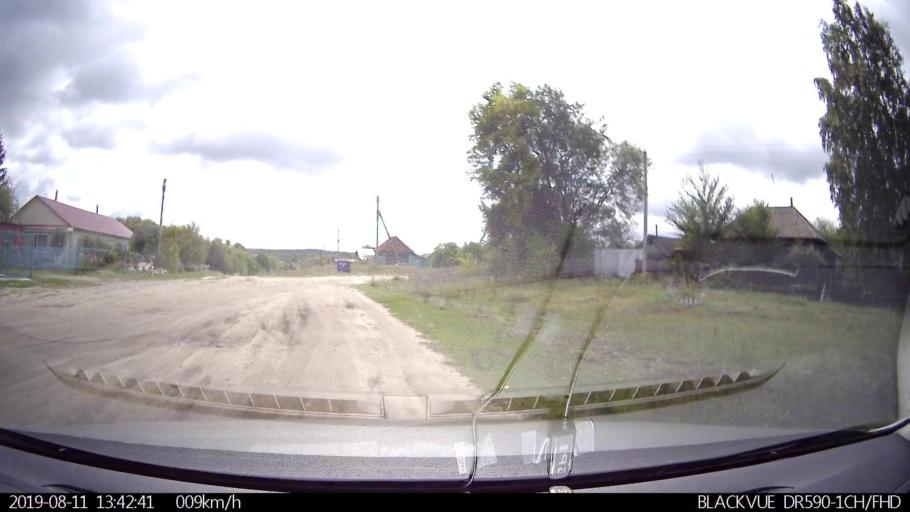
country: RU
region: Ulyanovsk
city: Ignatovka
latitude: 53.8562
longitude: 47.5751
